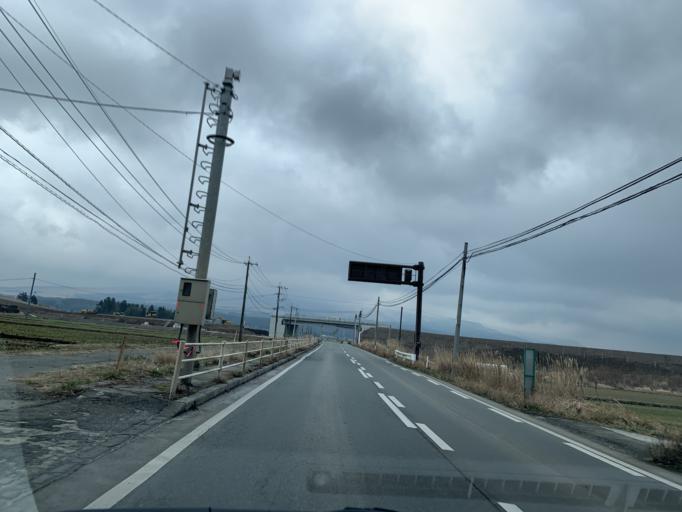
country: JP
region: Kumamoto
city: Aso
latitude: 32.9167
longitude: 130.9799
